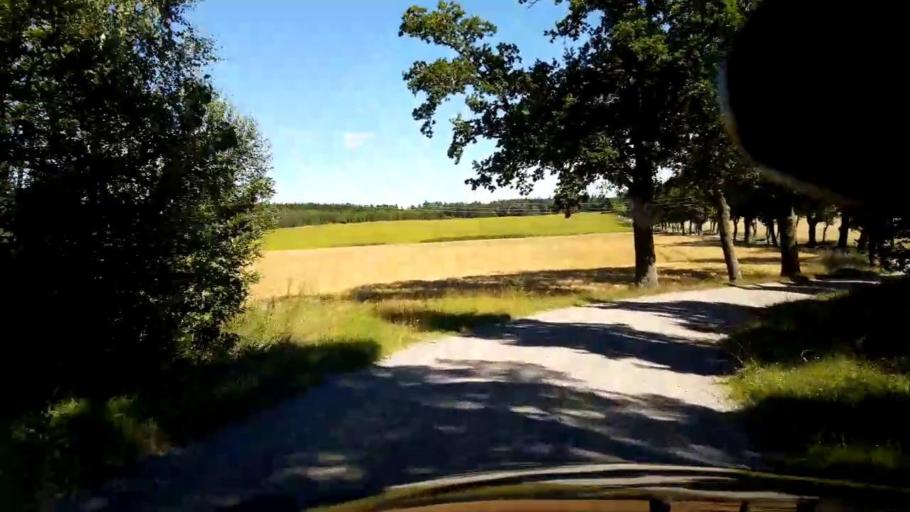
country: SE
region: Stockholm
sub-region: Sigtuna Kommun
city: Sigtuna
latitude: 59.6143
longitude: 17.6376
